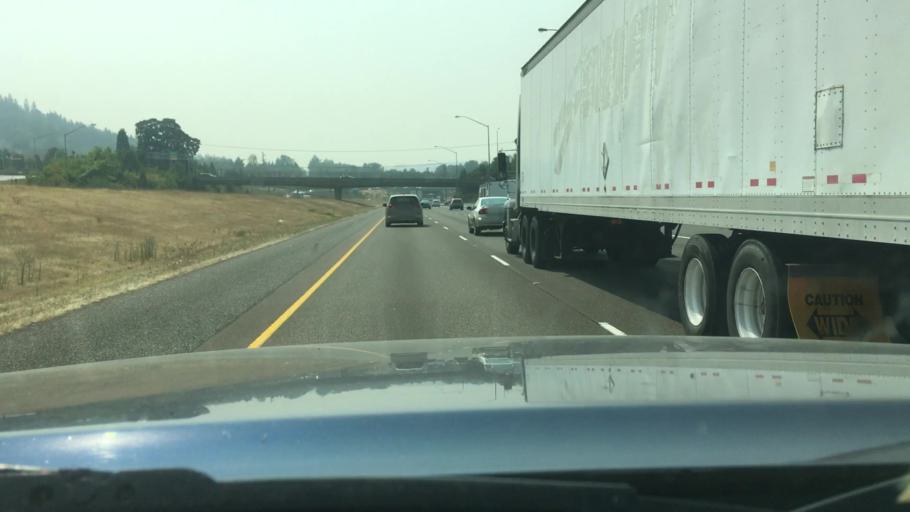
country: US
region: Oregon
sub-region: Clackamas County
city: Clackamas
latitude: 45.4356
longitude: -122.5672
